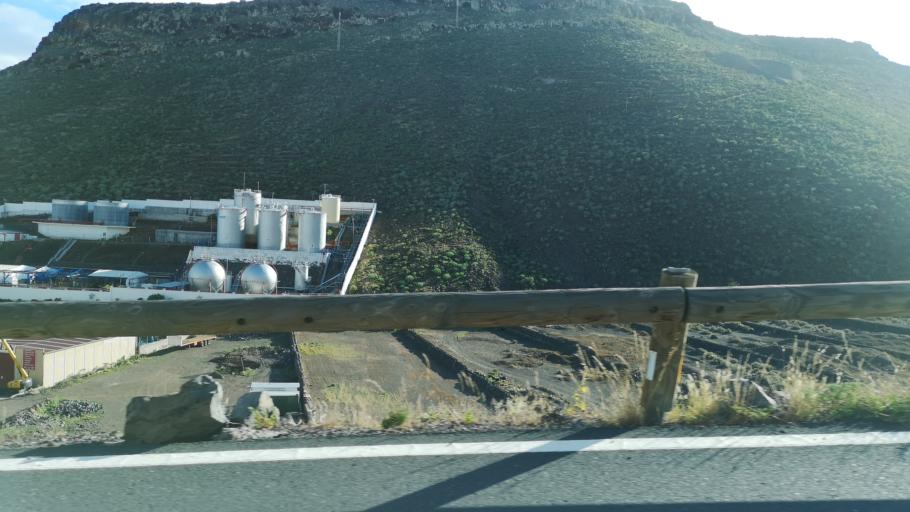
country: ES
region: Canary Islands
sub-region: Provincia de Santa Cruz de Tenerife
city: San Sebastian de la Gomera
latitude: 28.0900
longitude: -17.1186
